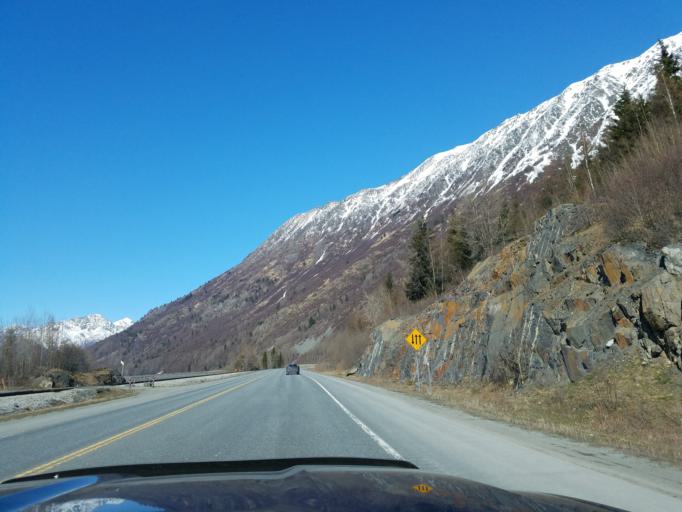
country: US
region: Alaska
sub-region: Anchorage Municipality
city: Girdwood
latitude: 60.9384
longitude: -149.3673
